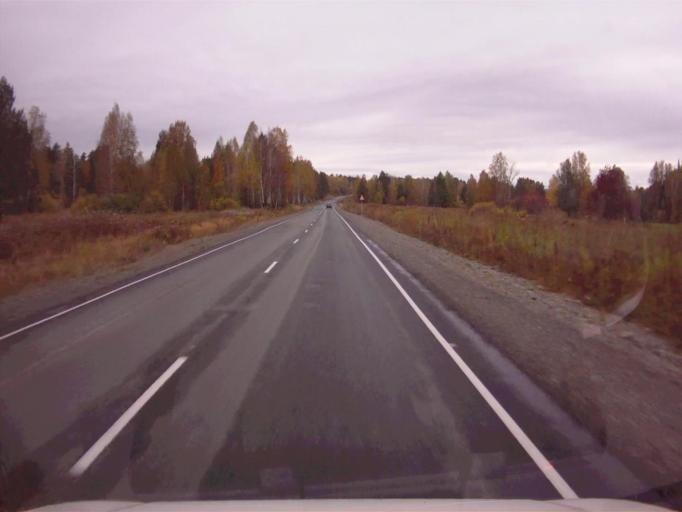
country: RU
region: Chelyabinsk
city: Nyazepetrovsk
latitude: 56.0448
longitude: 59.7635
